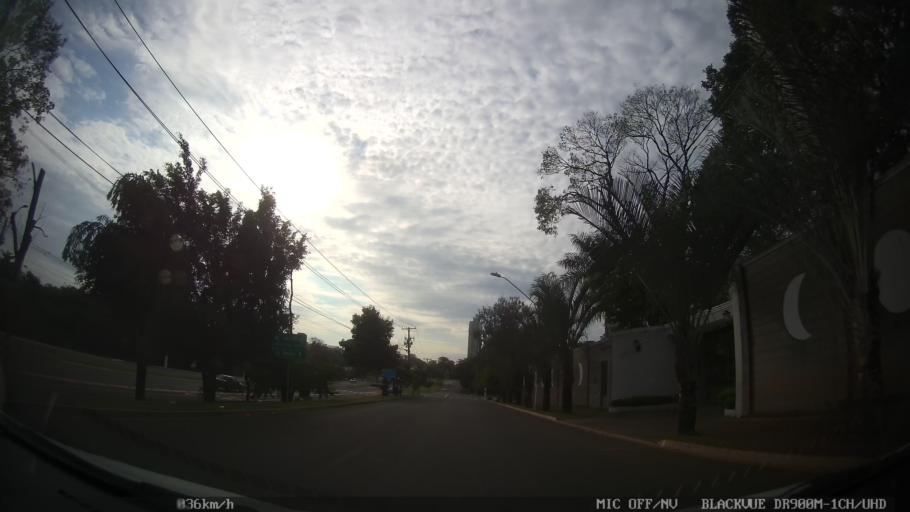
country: BR
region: Sao Paulo
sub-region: Santa Barbara D'Oeste
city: Santa Barbara d'Oeste
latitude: -22.7506
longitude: -47.3781
